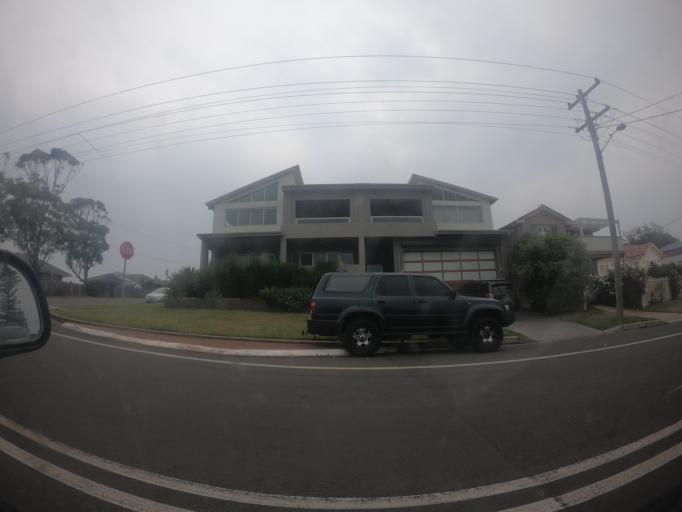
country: AU
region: New South Wales
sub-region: Shellharbour
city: Shellharbour Village
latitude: -34.5765
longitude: 150.8691
